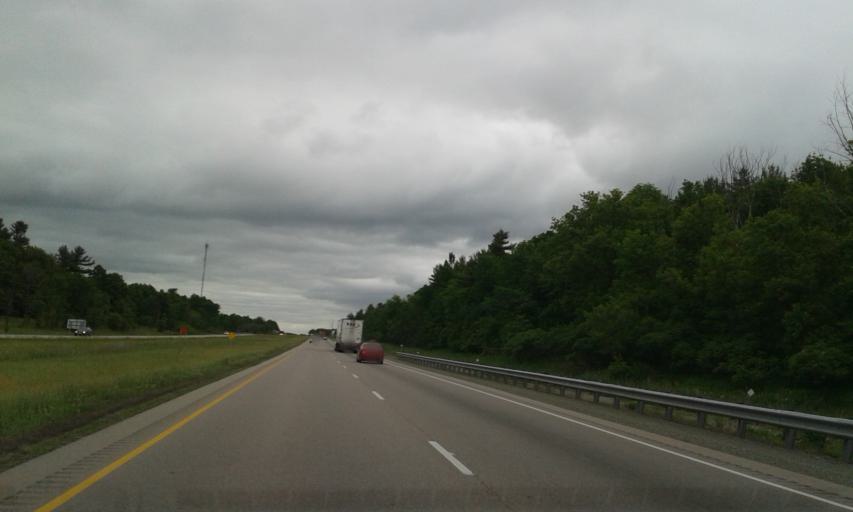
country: US
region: New York
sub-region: Jefferson County
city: Alexandria Bay
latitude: 44.4963
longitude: -75.8472
